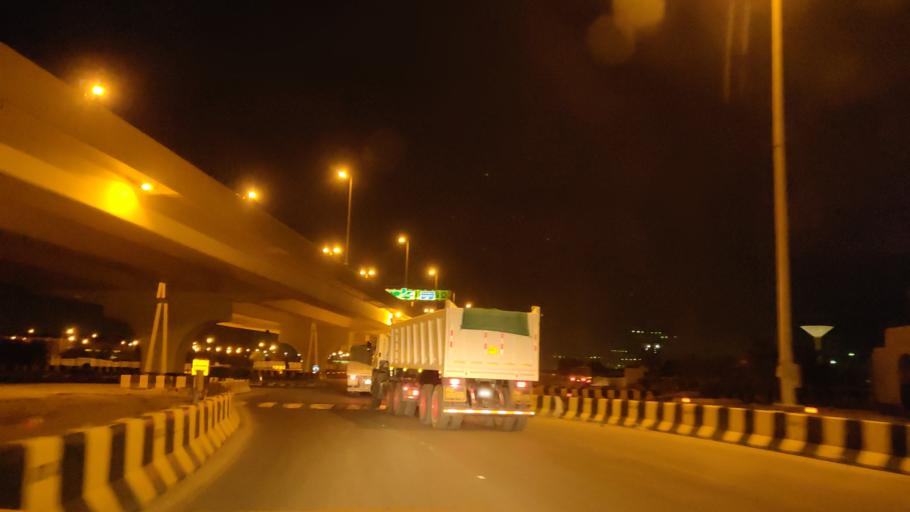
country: KW
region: Al Asimah
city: Ash Shamiyah
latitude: 29.3376
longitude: 47.9195
